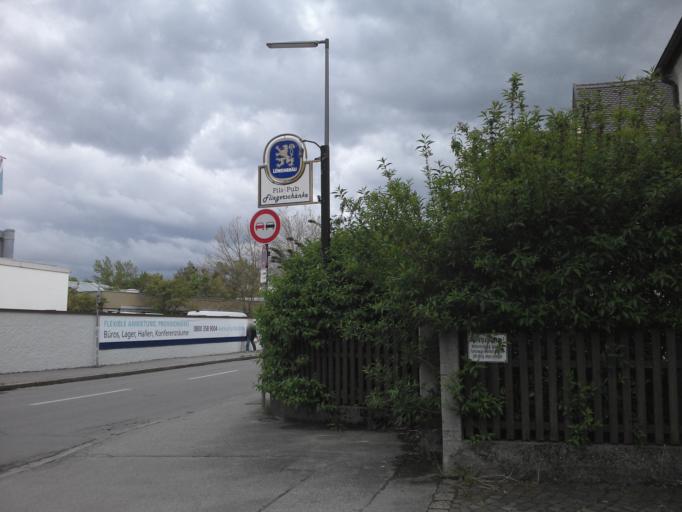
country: DE
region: Bavaria
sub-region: Upper Bavaria
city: Grafelfing
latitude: 48.1403
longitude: 11.4252
